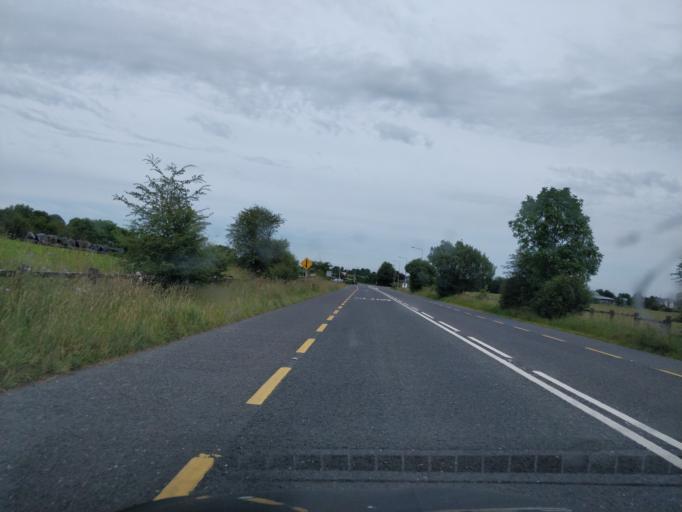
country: IE
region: Leinster
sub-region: Uibh Fhaili
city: Birr
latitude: 53.1500
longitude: -7.8388
